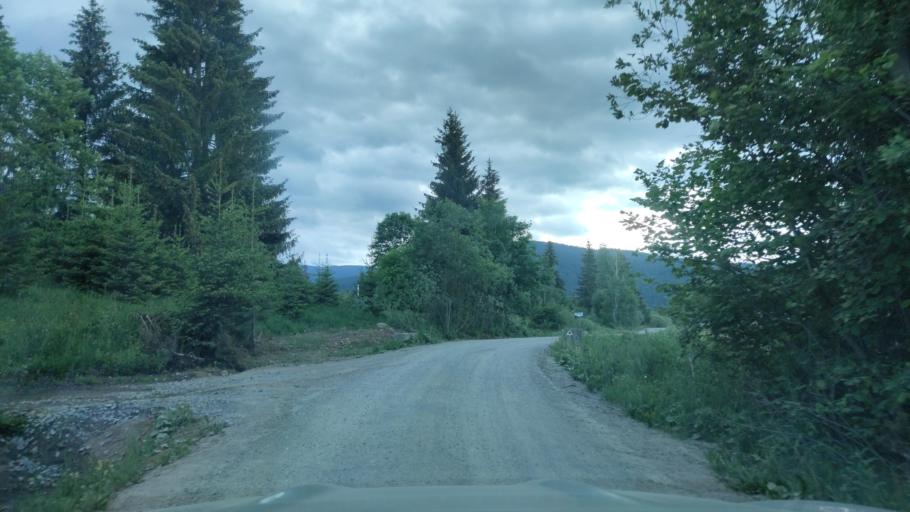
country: RO
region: Harghita
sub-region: Comuna Joseni
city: Joseni
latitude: 46.6687
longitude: 25.3740
